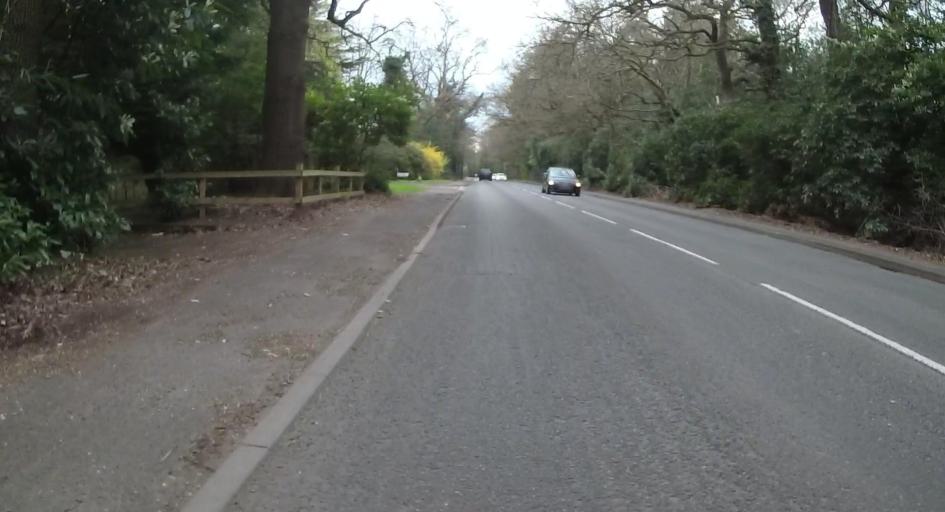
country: GB
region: England
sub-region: Surrey
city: West Byfleet
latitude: 51.3424
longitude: -0.5180
